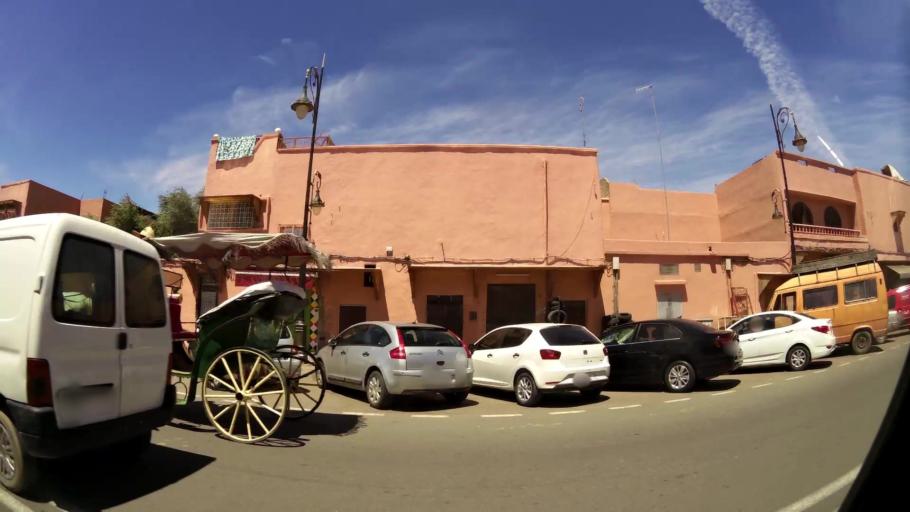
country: MA
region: Marrakech-Tensift-Al Haouz
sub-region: Marrakech
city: Marrakesh
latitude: 31.6143
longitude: -7.9778
